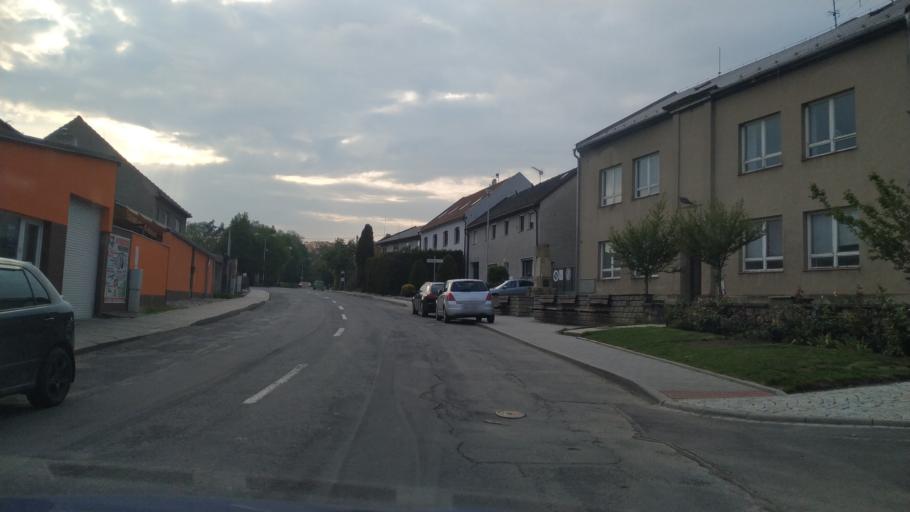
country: CZ
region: Olomoucky
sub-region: Okres Olomouc
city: Slatinice
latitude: 49.5508
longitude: 17.1120
